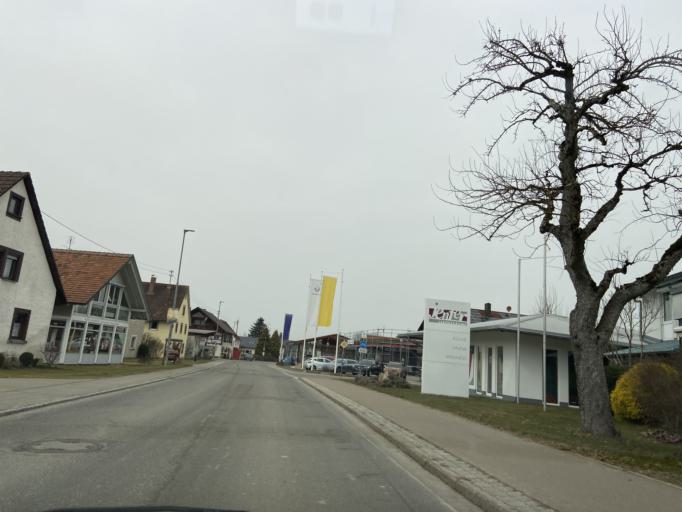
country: DE
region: Baden-Wuerttemberg
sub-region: Tuebingen Region
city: Pfullendorf
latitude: 47.8909
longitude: 9.3131
